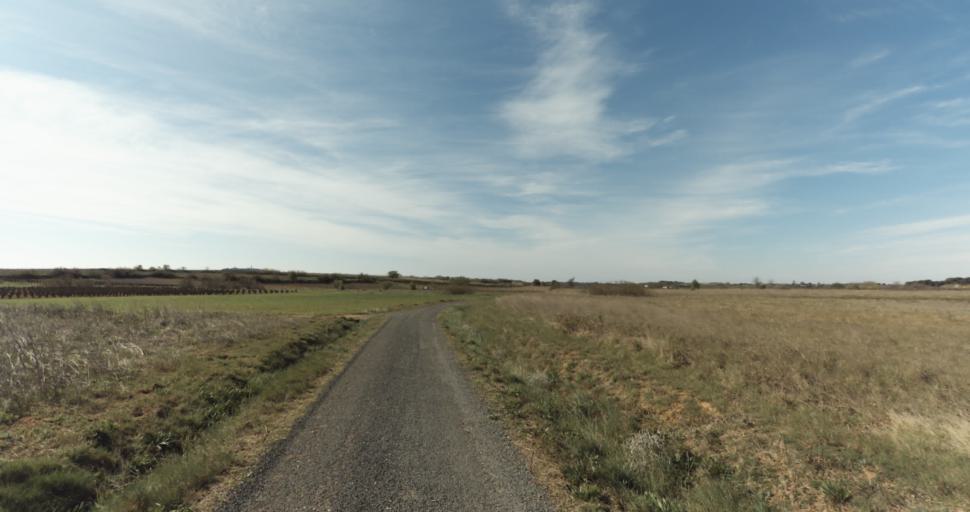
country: FR
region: Languedoc-Roussillon
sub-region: Departement de l'Herault
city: Marseillan
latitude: 43.3413
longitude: 3.5115
